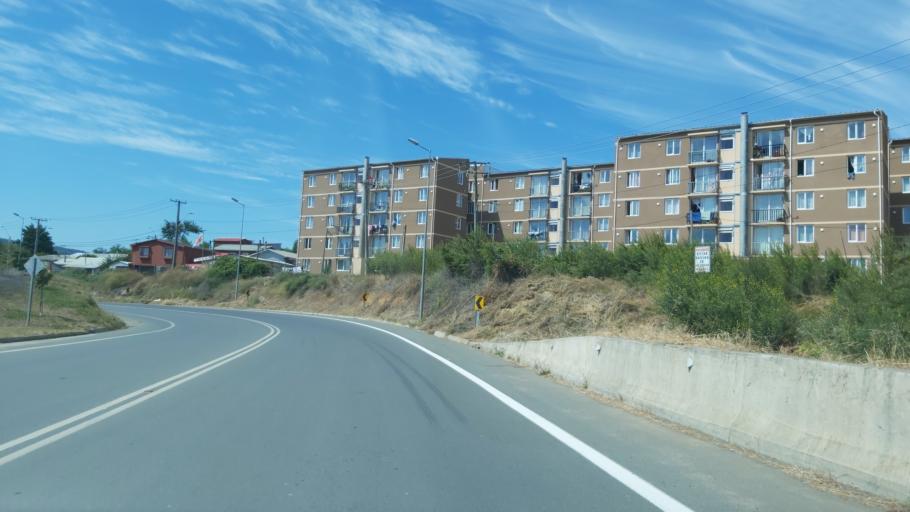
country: CL
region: Biobio
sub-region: Provincia de Concepcion
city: Coronel
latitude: -37.0244
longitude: -73.1367
